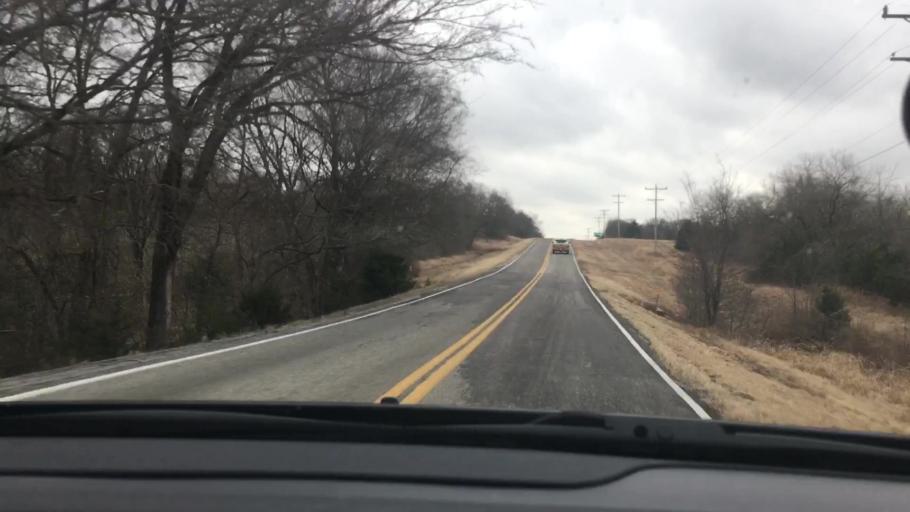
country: US
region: Oklahoma
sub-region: Johnston County
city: Tishomingo
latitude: 34.1512
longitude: -96.5565
